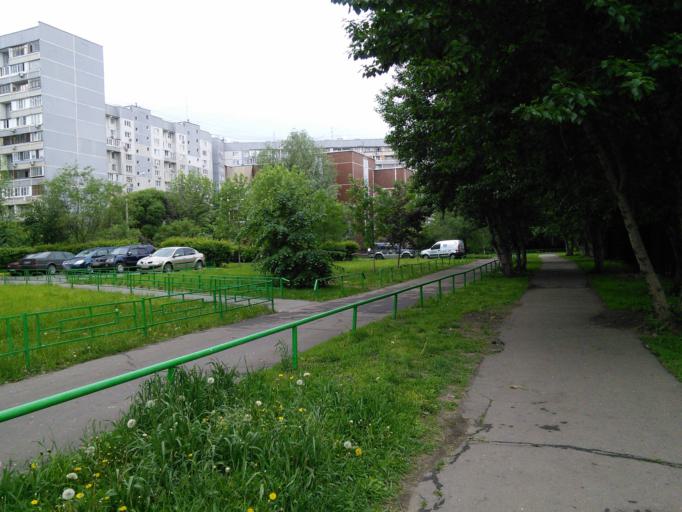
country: RU
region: Moscow
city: Brateyevo
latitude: 55.6506
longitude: 37.7539
